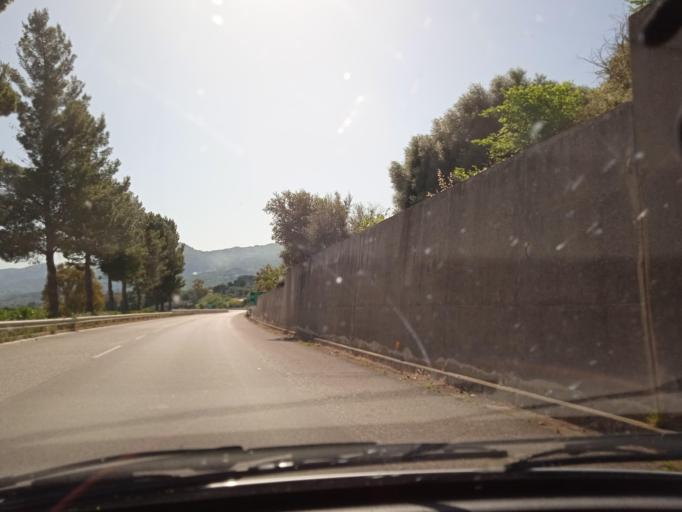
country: IT
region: Sicily
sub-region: Messina
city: Sant'Agata di Militello
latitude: 38.0607
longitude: 14.6292
